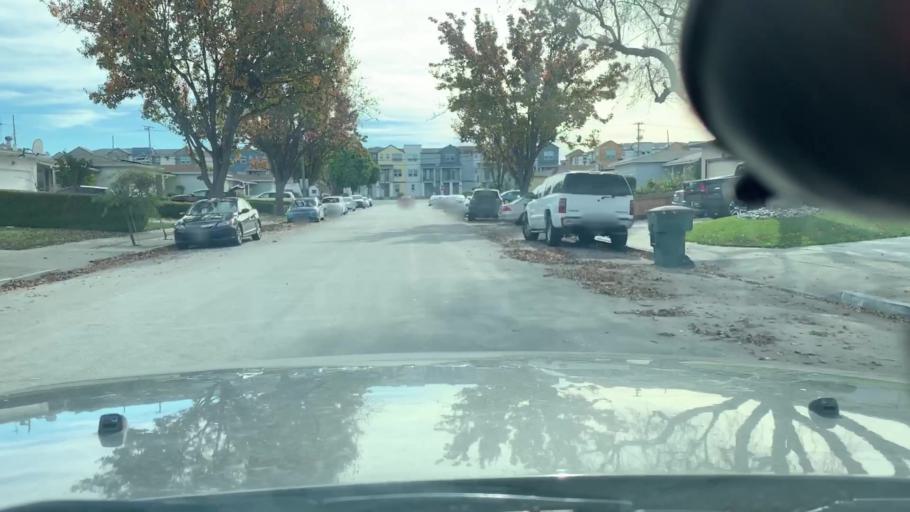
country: US
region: California
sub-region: Santa Clara County
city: Sunnyvale
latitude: 37.3897
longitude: -122.0063
